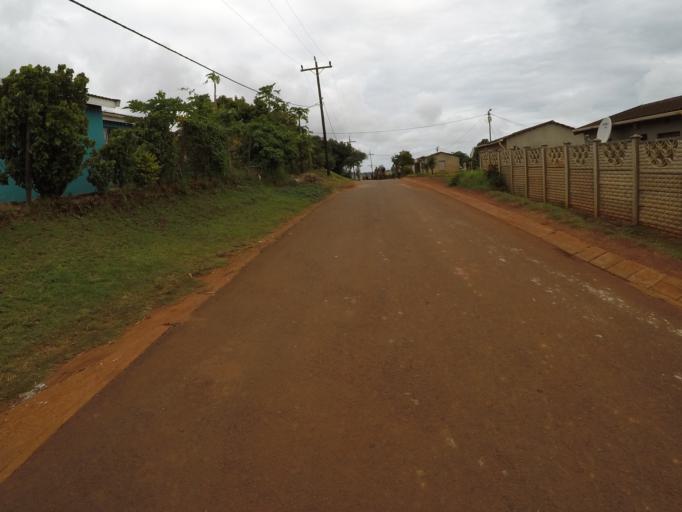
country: ZA
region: KwaZulu-Natal
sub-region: uThungulu District Municipality
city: Empangeni
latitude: -28.7732
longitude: 31.8789
